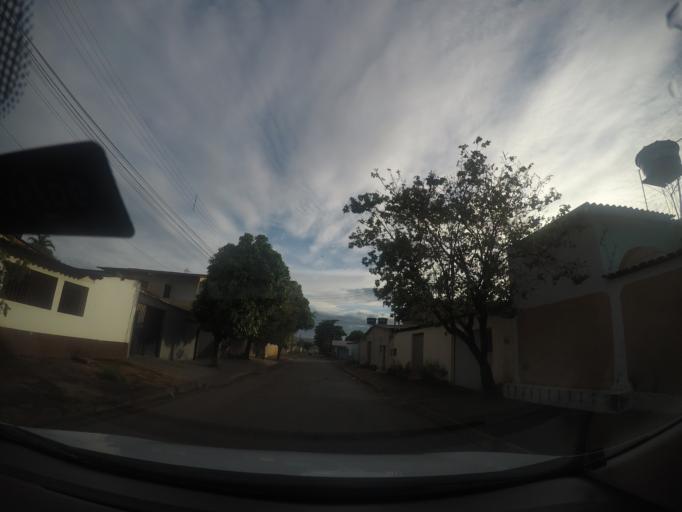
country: BR
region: Goias
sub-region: Goiania
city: Goiania
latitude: -16.6435
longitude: -49.3210
